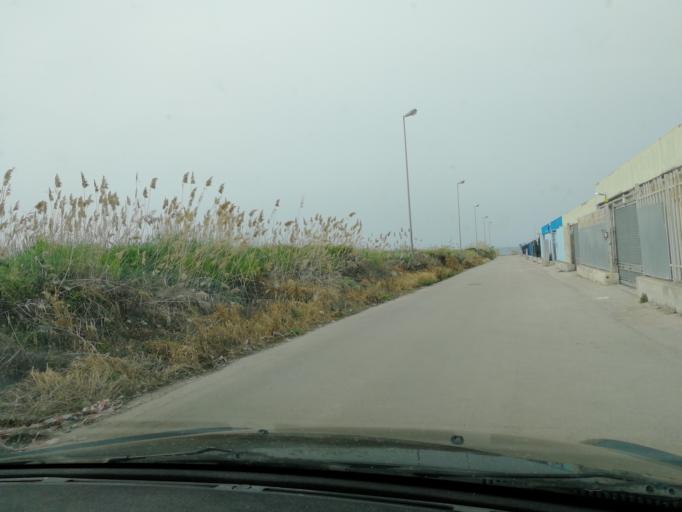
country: IT
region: Apulia
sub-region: Provincia di Barletta - Andria - Trani
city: Barletta
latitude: 41.3136
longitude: 16.3106
